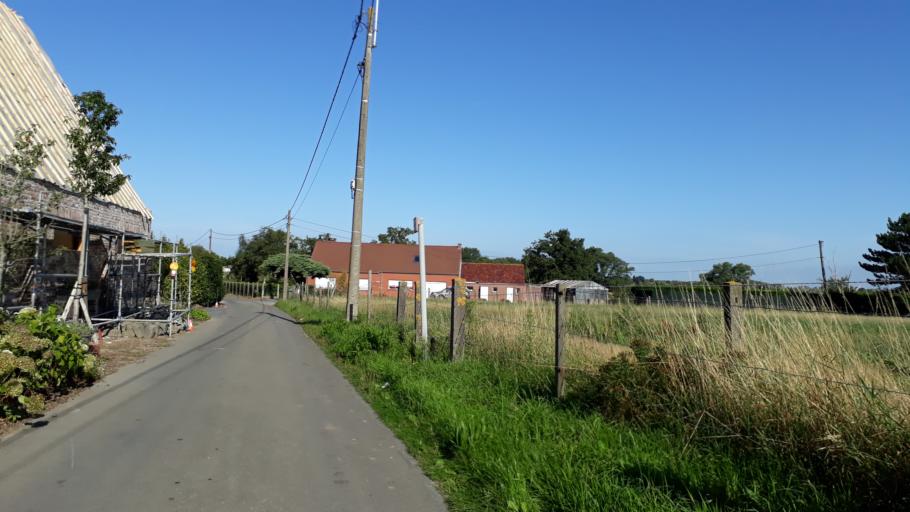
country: BE
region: Flanders
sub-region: Provincie West-Vlaanderen
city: Torhout
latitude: 51.0870
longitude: 3.1316
